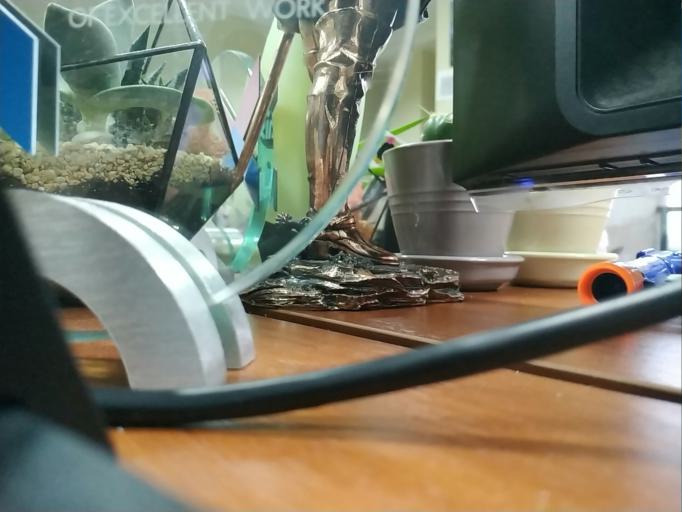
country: RU
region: Moskovskaya
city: Lobnya
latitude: 56.0149
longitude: 37.4829
